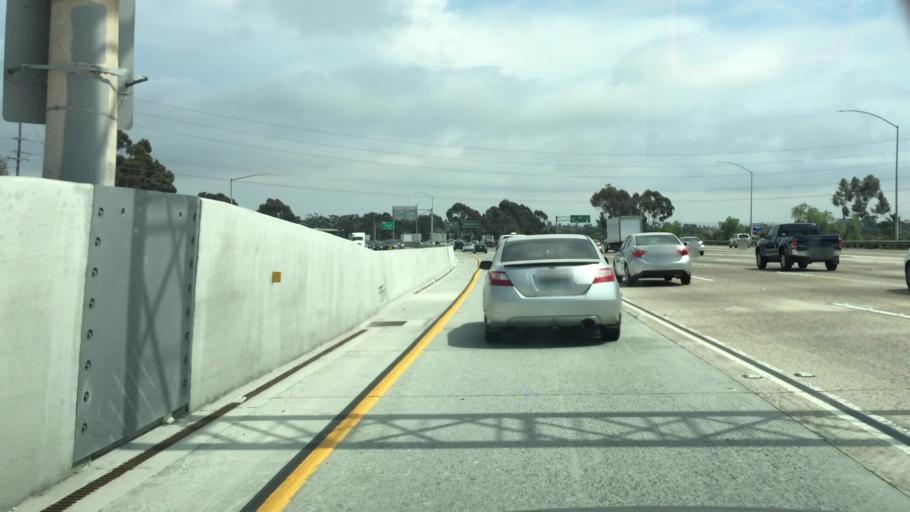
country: US
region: California
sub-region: San Diego County
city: National City
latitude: 32.6646
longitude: -117.0794
